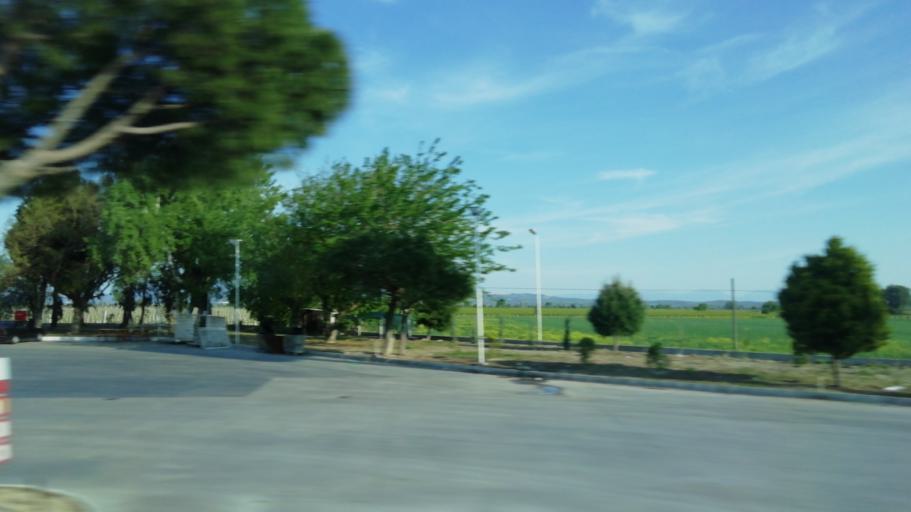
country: TR
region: Manisa
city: Saruhanli
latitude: 38.7413
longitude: 27.6040
